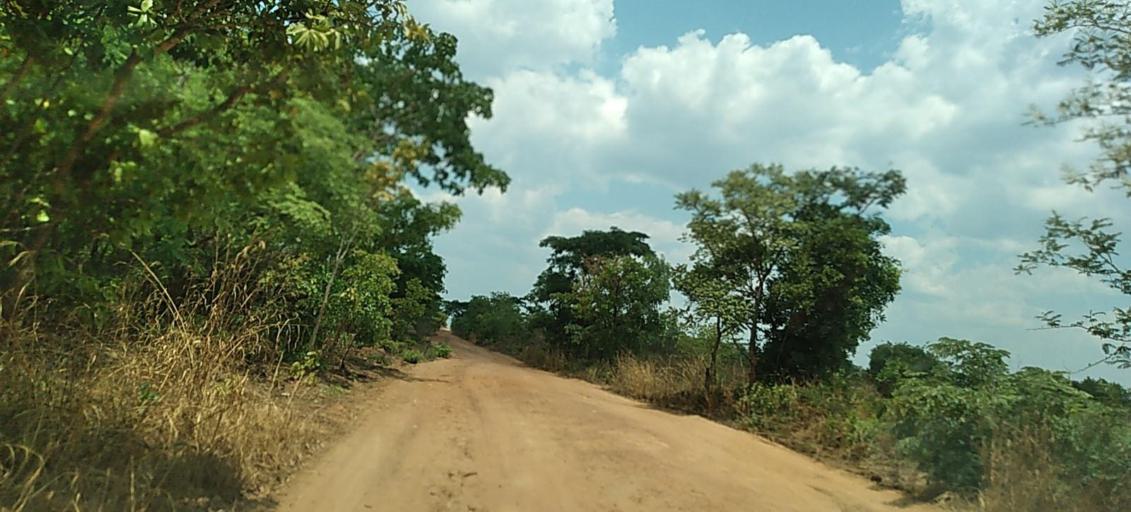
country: ZM
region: Copperbelt
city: Luanshya
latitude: -13.3777
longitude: 28.4305
